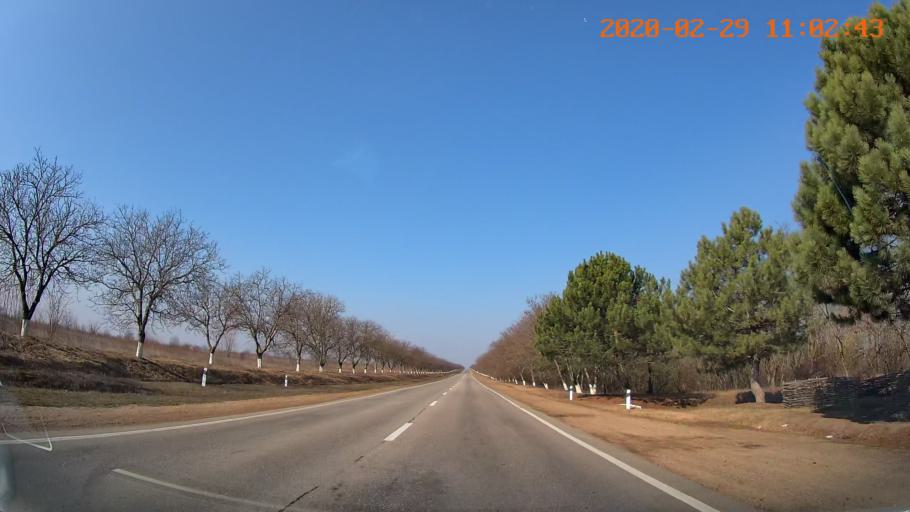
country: MD
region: Telenesti
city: Grigoriopol
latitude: 47.1744
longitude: 29.2325
